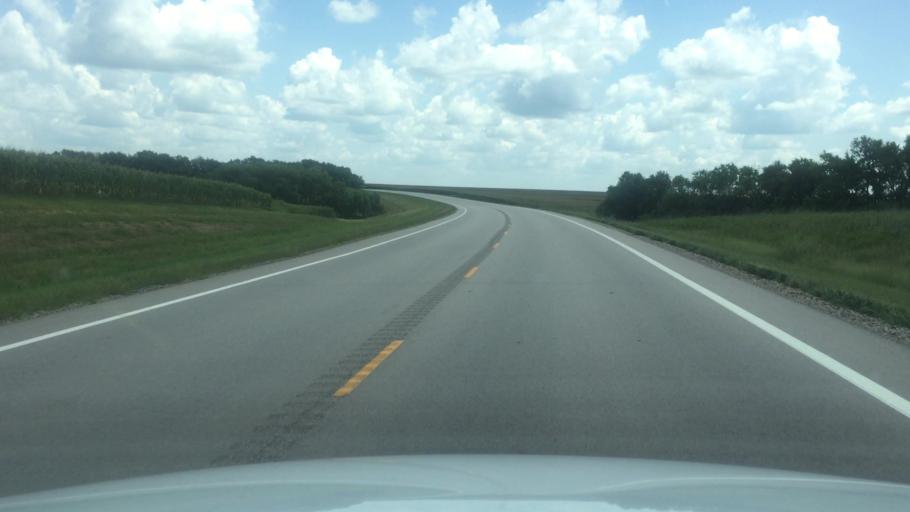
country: US
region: Kansas
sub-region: Brown County
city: Horton
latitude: 39.6611
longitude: -95.4097
